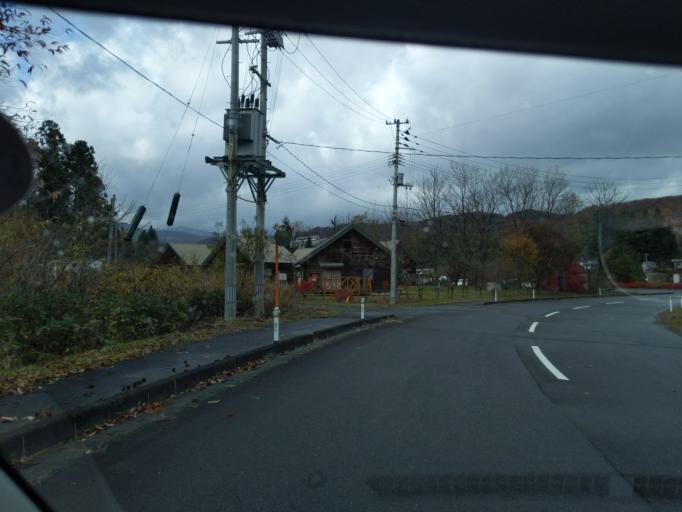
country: JP
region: Iwate
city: Mizusawa
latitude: 39.1146
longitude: 140.9462
